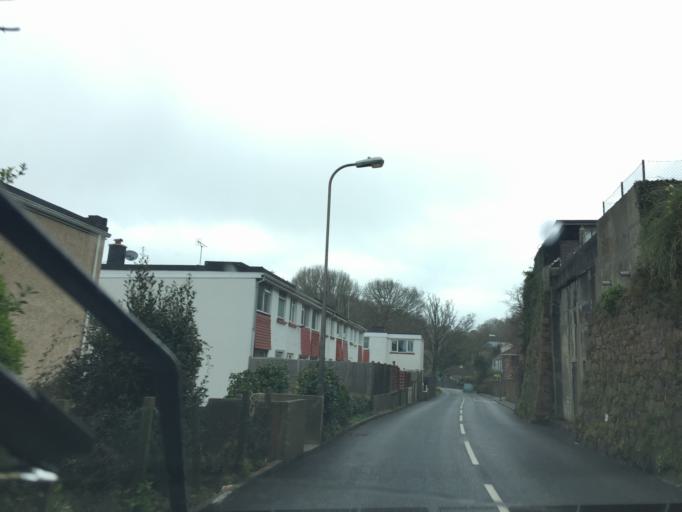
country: JE
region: St Helier
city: Saint Helier
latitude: 49.2035
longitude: -2.1552
